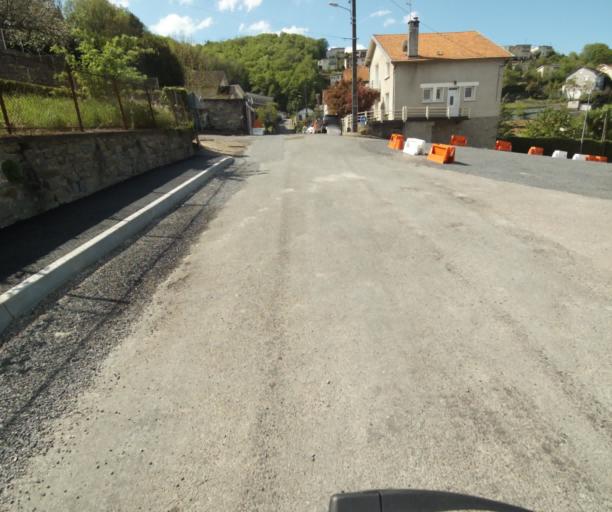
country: FR
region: Limousin
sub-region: Departement de la Correze
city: Tulle
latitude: 45.2621
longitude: 1.7642
